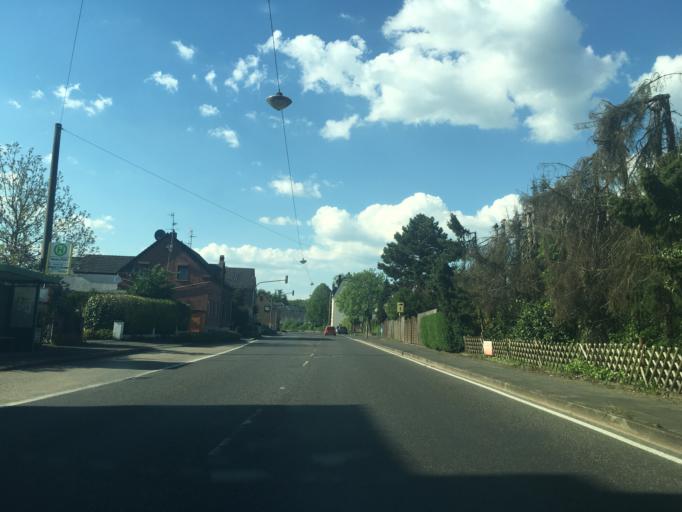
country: DE
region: North Rhine-Westphalia
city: Haan
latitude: 51.1762
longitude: 6.9883
